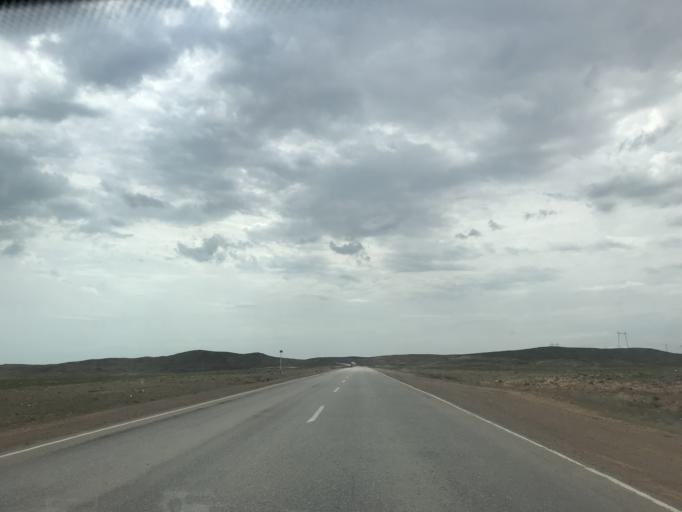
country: KZ
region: Zhambyl
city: Mynaral
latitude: 45.5153
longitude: 73.4936
